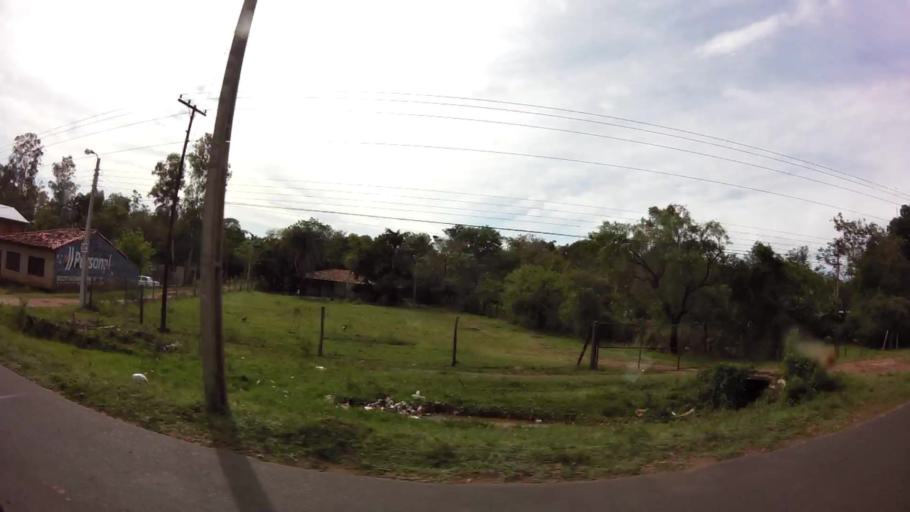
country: PY
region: Central
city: Limpio
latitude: -25.1455
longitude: -57.4585
